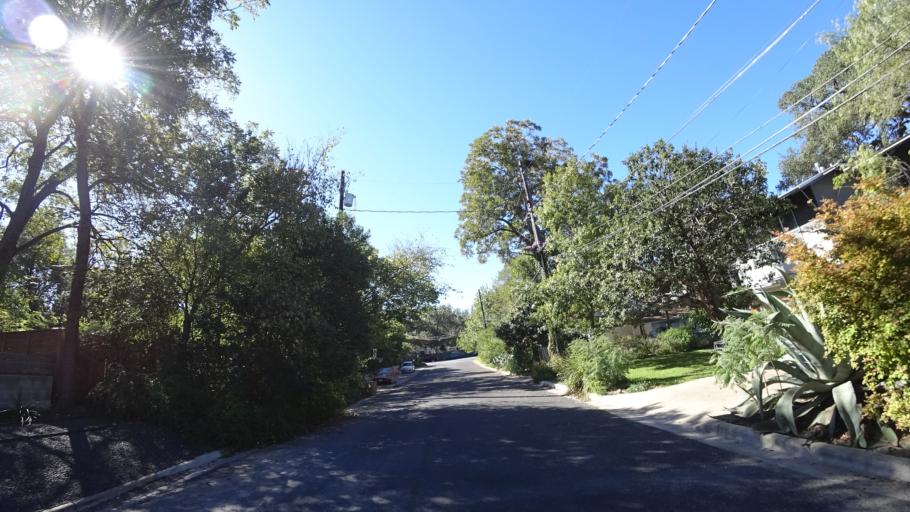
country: US
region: Texas
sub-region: Travis County
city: Austin
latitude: 30.2455
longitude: -97.7536
